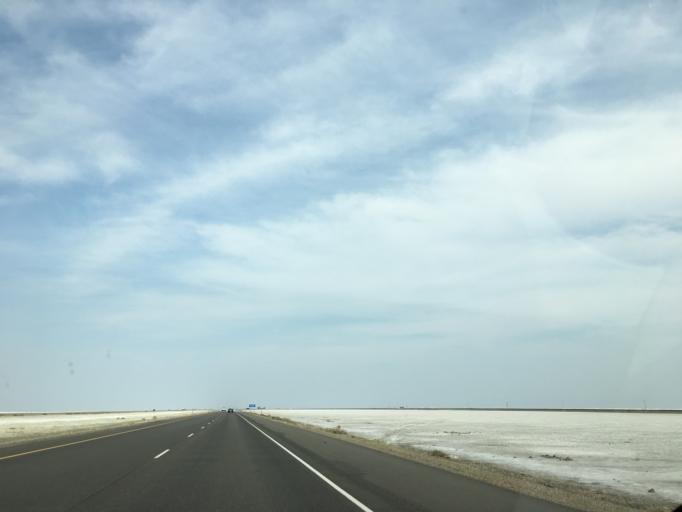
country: US
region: Utah
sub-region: Tooele County
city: Wendover
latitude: 40.7392
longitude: -113.8868
